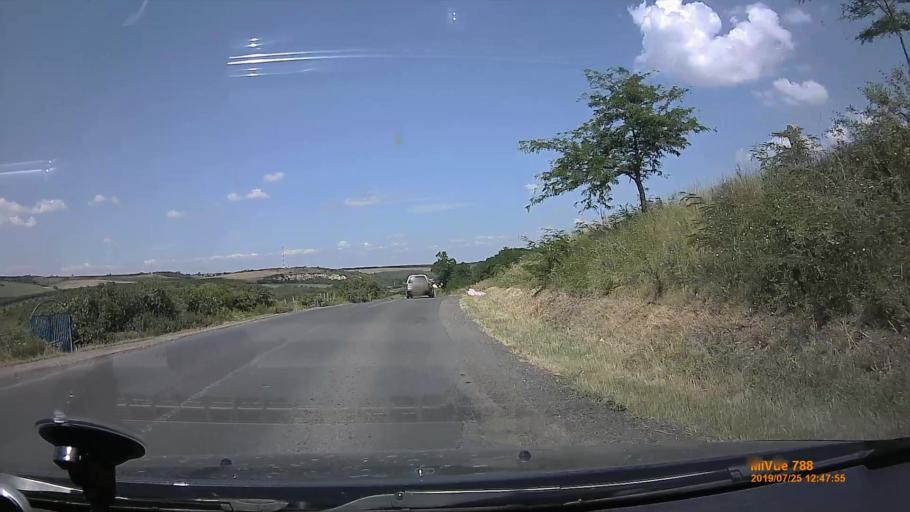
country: HU
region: Borsod-Abauj-Zemplen
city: Abaujszanto
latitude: 48.2647
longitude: 21.1850
